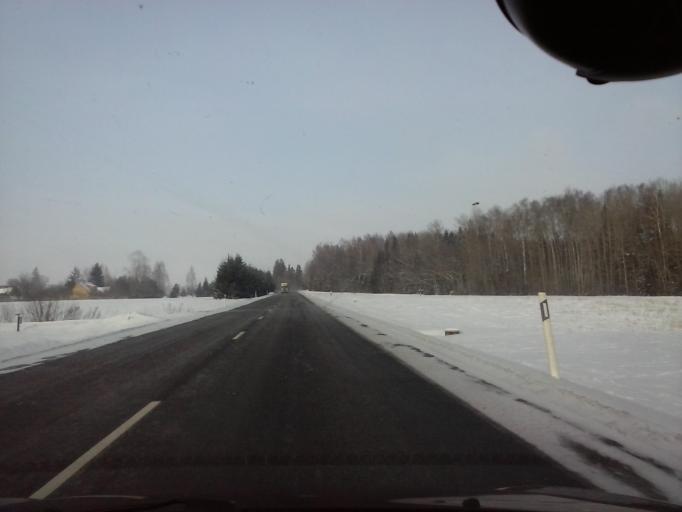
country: EE
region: Viljandimaa
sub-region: Abja vald
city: Abja-Paluoja
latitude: 58.3031
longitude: 25.2993
